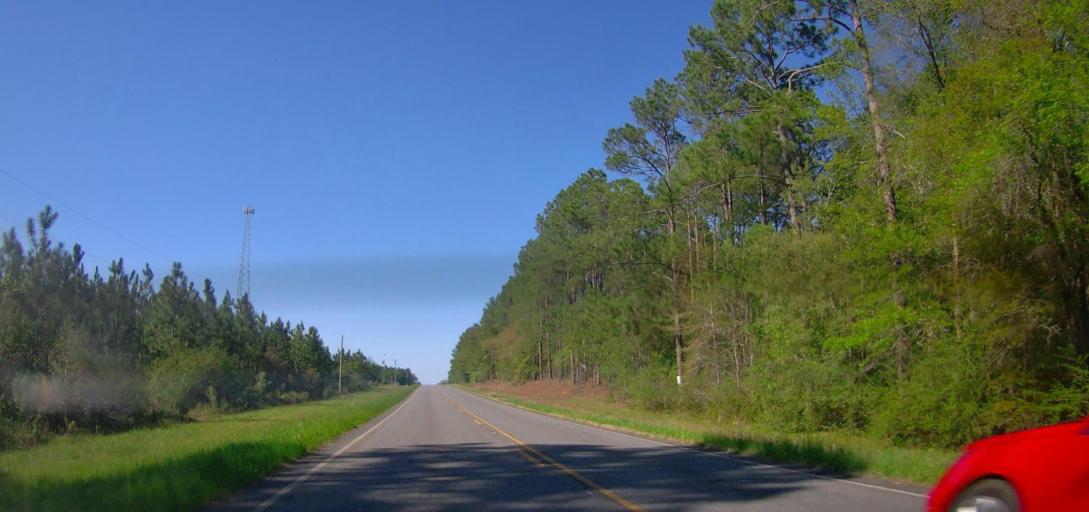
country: US
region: Georgia
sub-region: Wilcox County
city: Rochelle
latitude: 32.0403
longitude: -83.5037
